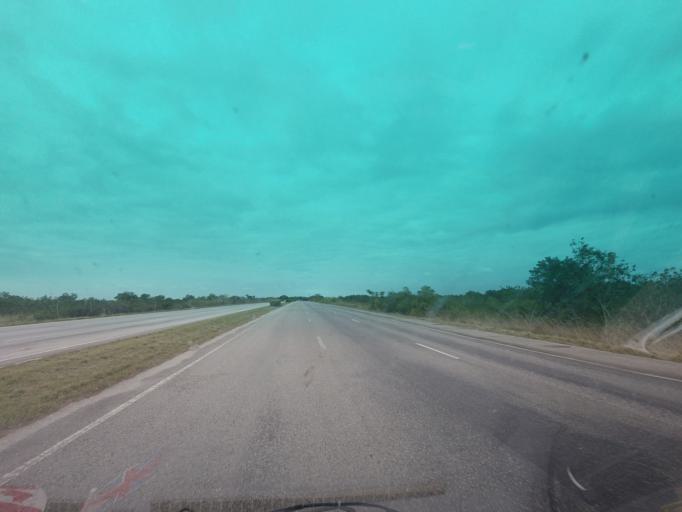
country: CU
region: Mayabeque
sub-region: Municipio de San Nicolas
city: San Nicolas de Bari
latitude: 22.7873
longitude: -81.8451
